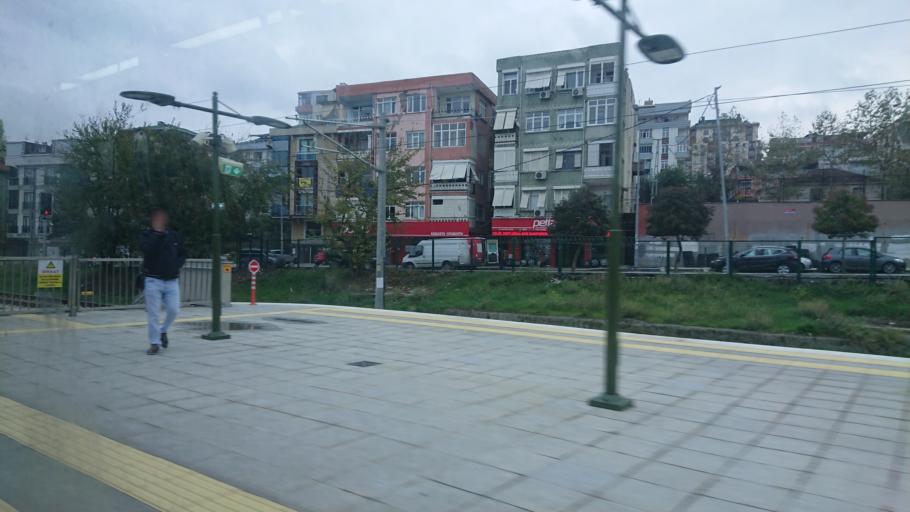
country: TR
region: Istanbul
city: Mahmutbey
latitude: 41.0071
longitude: 28.7744
